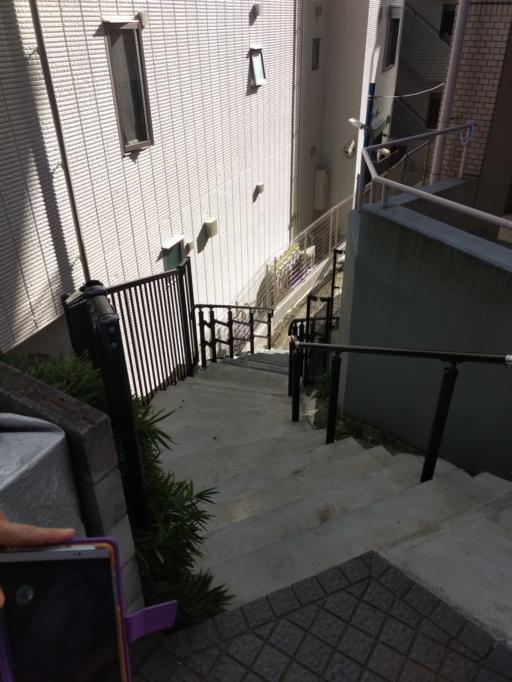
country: JP
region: Tokyo
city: Tokyo
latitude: 35.7055
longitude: 139.6865
